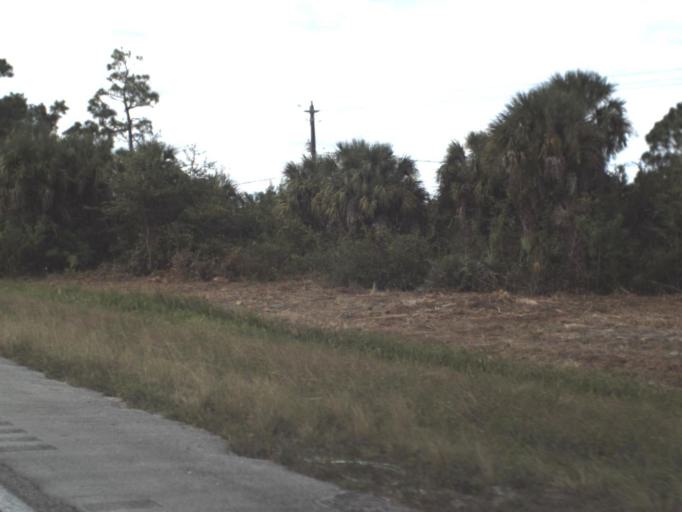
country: US
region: Florida
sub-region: Brevard County
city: Sharpes
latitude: 28.4043
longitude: -80.7765
